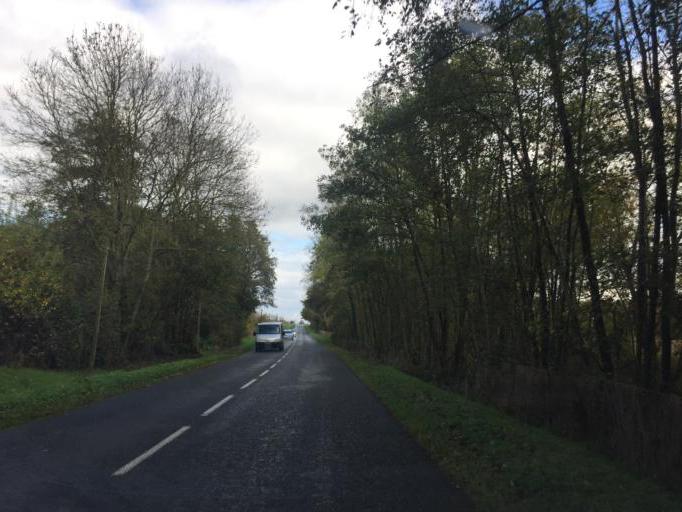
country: FR
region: Rhone-Alpes
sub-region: Departement de l'Ain
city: Mionnay
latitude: 45.9157
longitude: 4.9235
